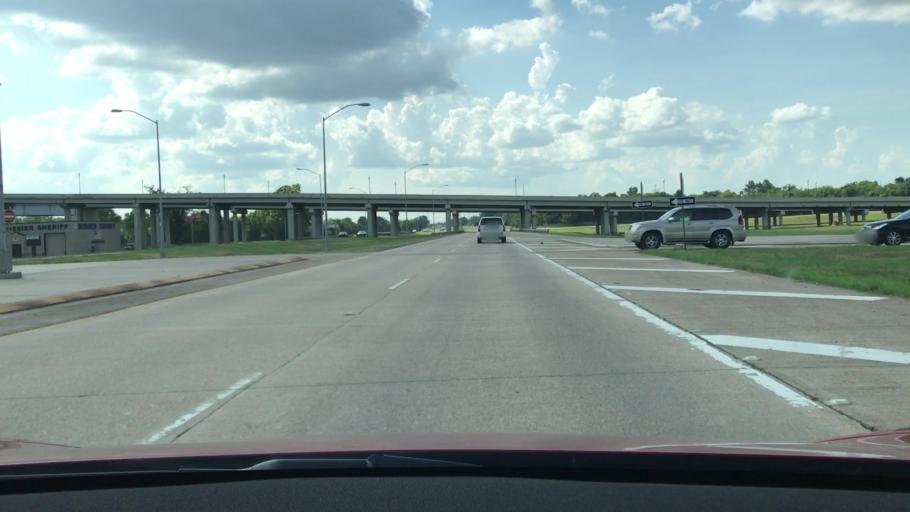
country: US
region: Louisiana
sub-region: Bossier Parish
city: Bossier City
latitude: 32.4931
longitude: -93.6947
